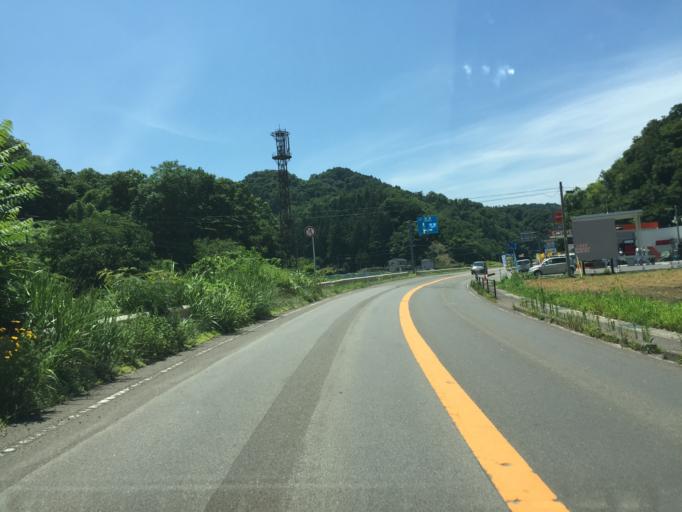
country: JP
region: Fukushima
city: Hobaramachi
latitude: 37.7585
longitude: 140.5617
